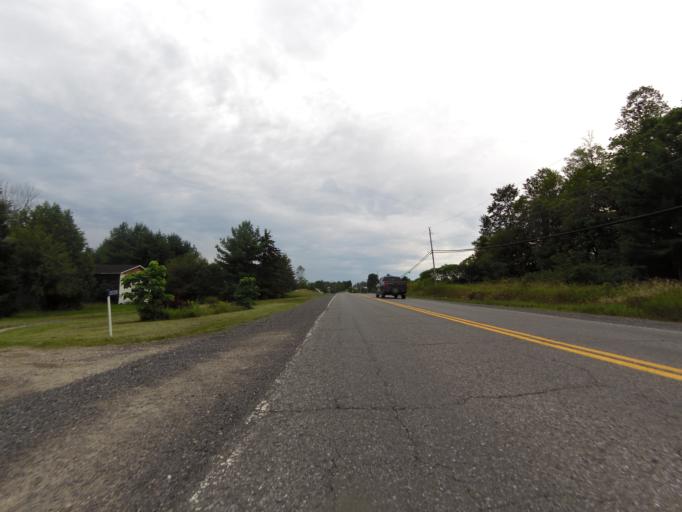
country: CA
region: Ontario
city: Carleton Place
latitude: 45.1602
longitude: -76.2942
